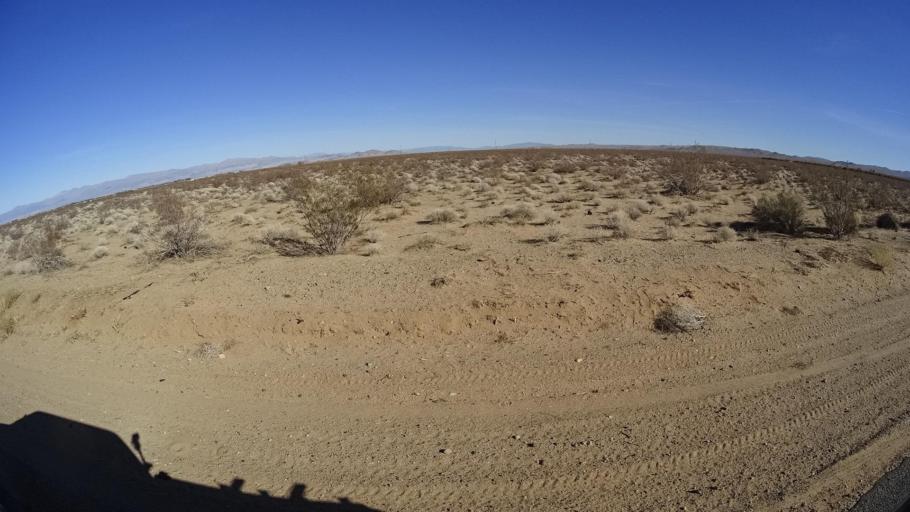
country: US
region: California
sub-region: Kern County
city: Inyokern
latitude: 35.5981
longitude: -117.7969
